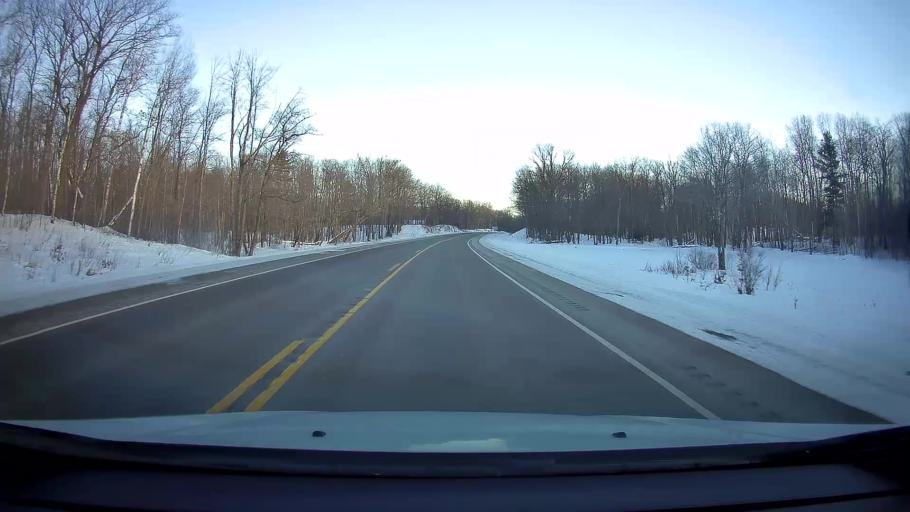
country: US
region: Wisconsin
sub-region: Washburn County
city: Shell Lake
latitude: 45.6708
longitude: -91.9934
